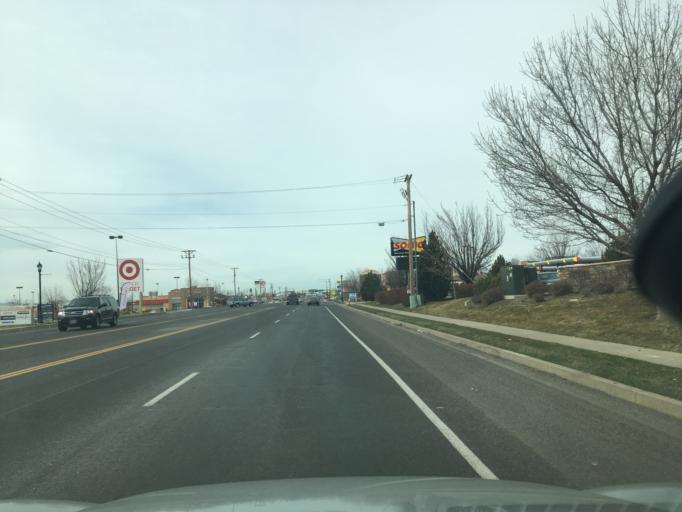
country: US
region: Utah
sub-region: Davis County
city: Hill Air Force Bace
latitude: 41.0892
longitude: -111.9800
